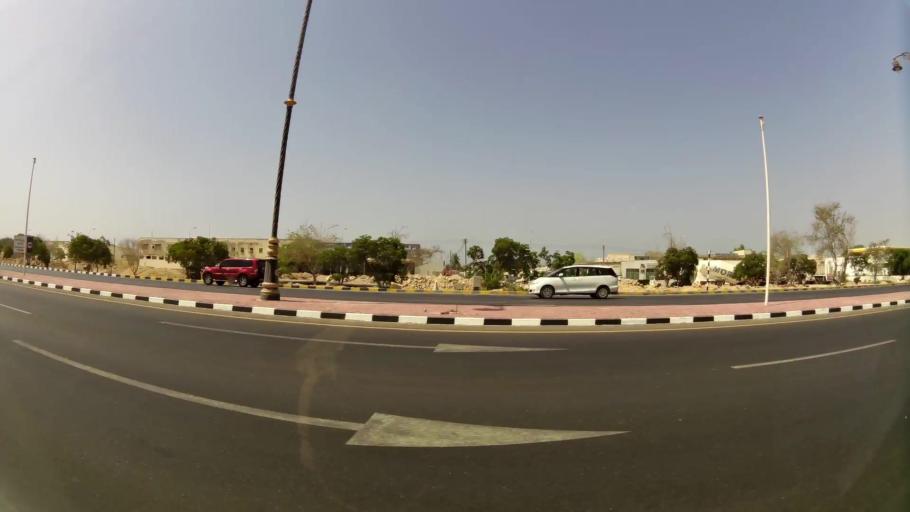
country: OM
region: Zufar
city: Salalah
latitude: 17.0251
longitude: 54.1165
